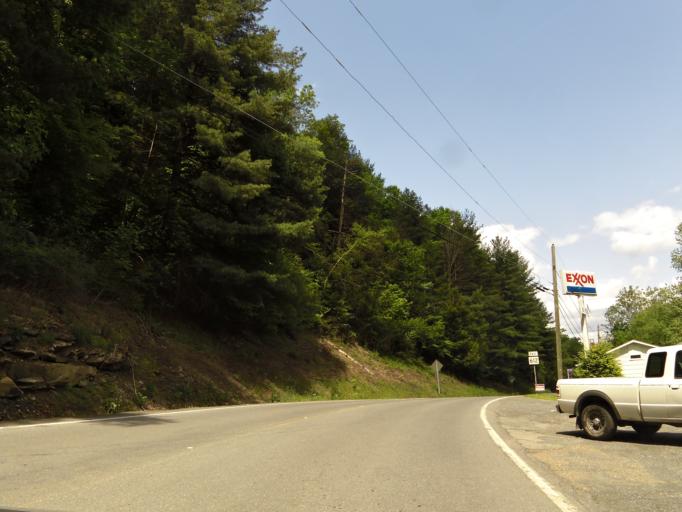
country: US
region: West Virginia
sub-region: Fayette County
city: Oak Hill
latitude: 37.9754
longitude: -81.2833
